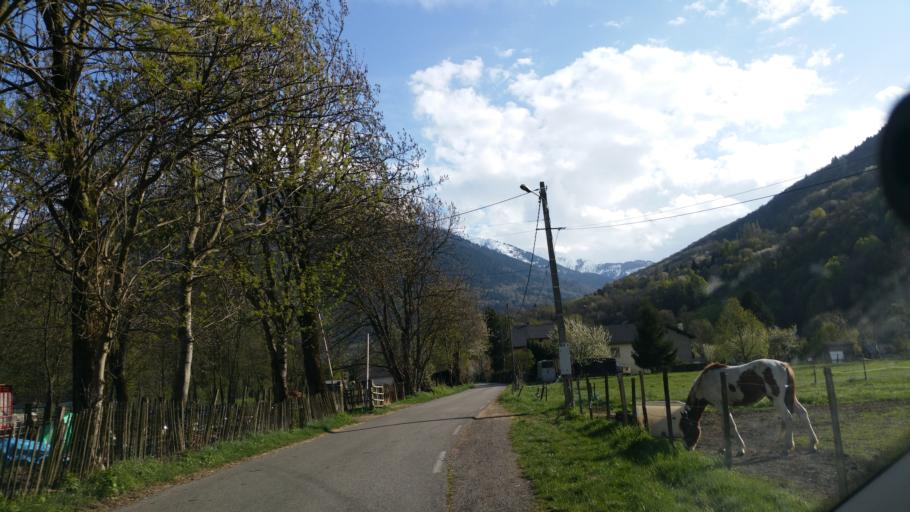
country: FR
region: Rhone-Alpes
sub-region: Departement de la Savoie
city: Saint-Etienne-de-Cuines
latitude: 45.3478
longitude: 6.2917
